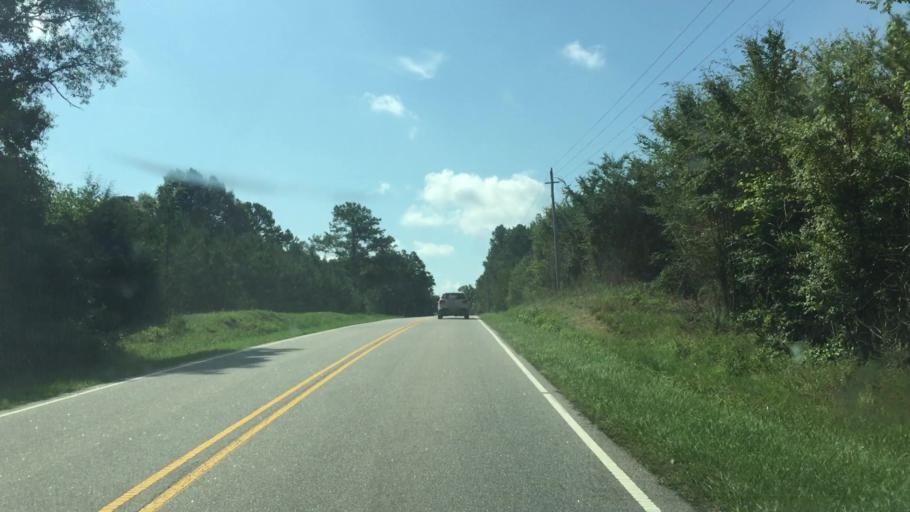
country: US
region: North Carolina
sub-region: Anson County
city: Burnsville
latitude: 35.0591
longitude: -80.2754
